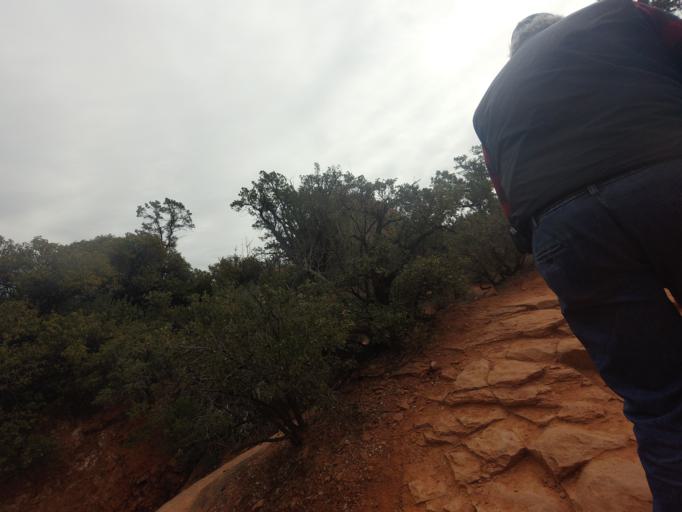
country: US
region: Arizona
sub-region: Yavapai County
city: Village of Oak Creek (Big Park)
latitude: 34.8030
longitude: -111.7653
